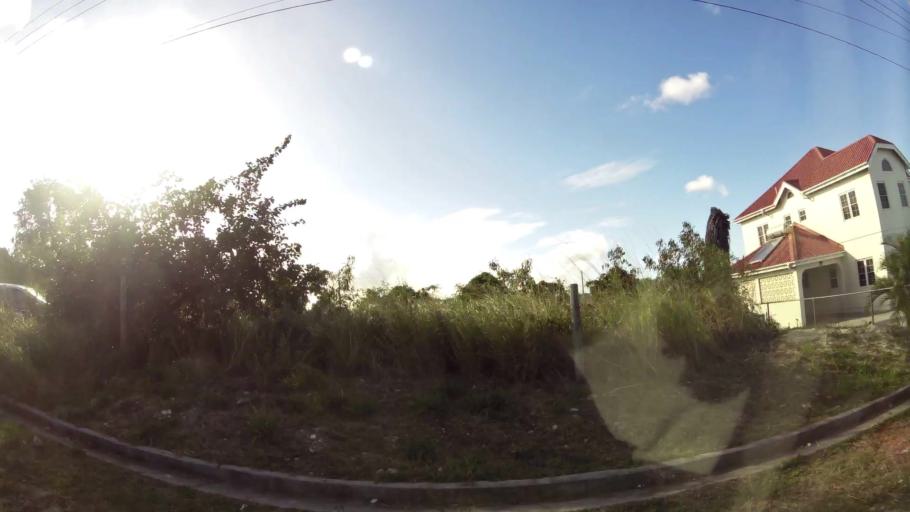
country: AG
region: Saint John
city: Potters Village
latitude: 17.0944
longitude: -61.8043
